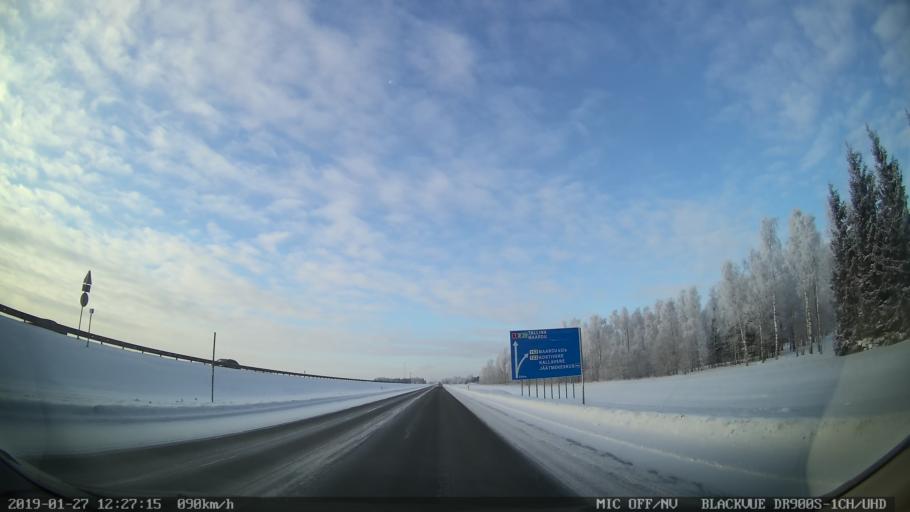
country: EE
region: Harju
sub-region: Maardu linn
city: Maardu
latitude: 59.4514
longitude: 25.0480
